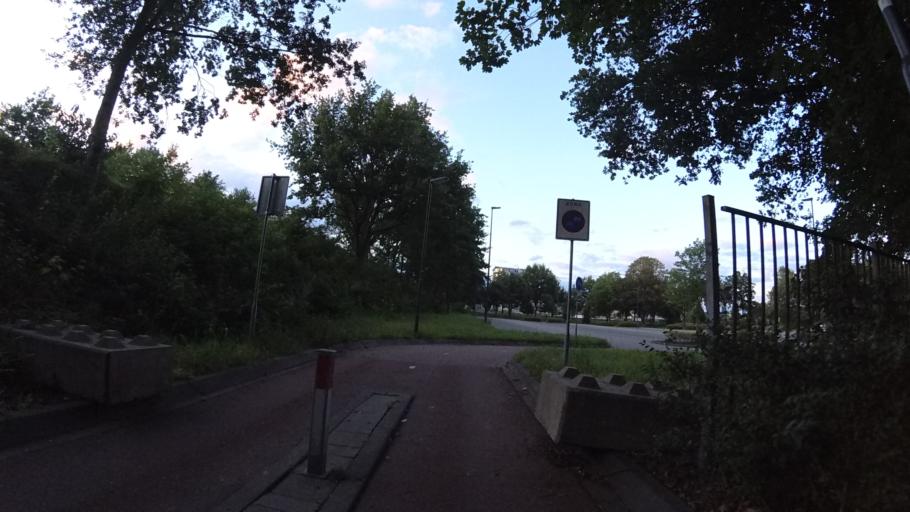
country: NL
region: North Brabant
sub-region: Gemeente Oosterhout
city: Oosterhout
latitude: 51.6349
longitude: 4.8446
